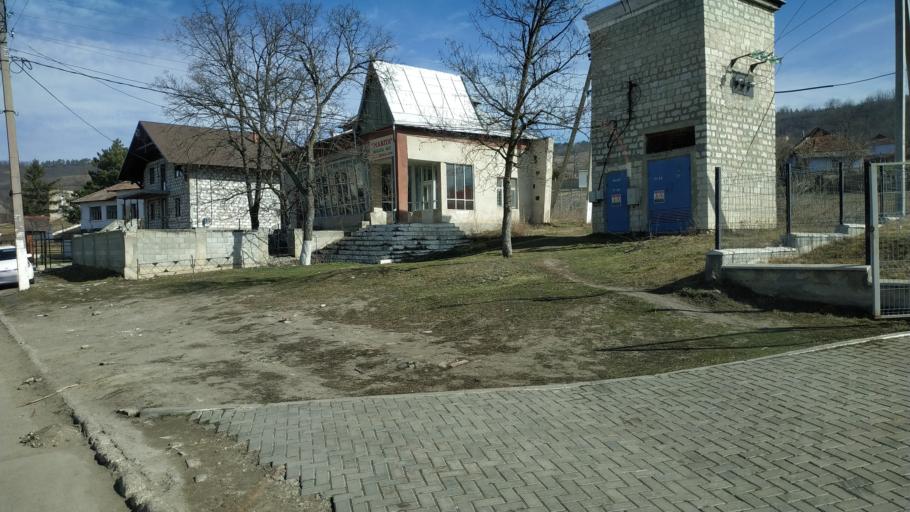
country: MD
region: Nisporeni
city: Nisporeni
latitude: 47.0773
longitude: 28.2613
